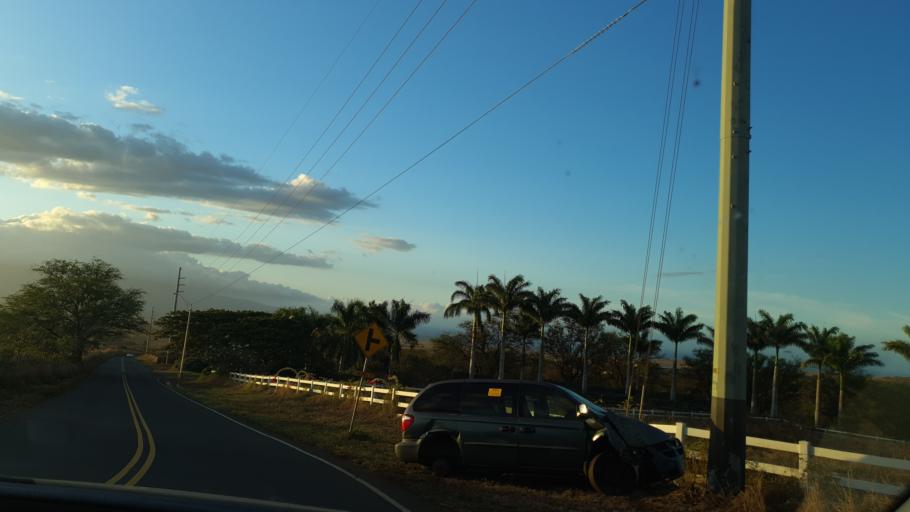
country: US
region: Hawaii
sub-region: Maui County
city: Pukalani
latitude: 20.7992
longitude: -156.3721
